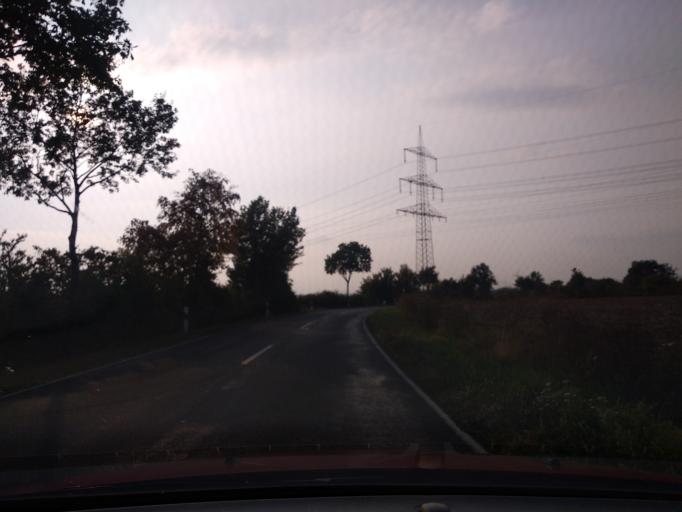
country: DE
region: North Rhine-Westphalia
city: Beverungen
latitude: 51.6294
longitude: 9.3394
